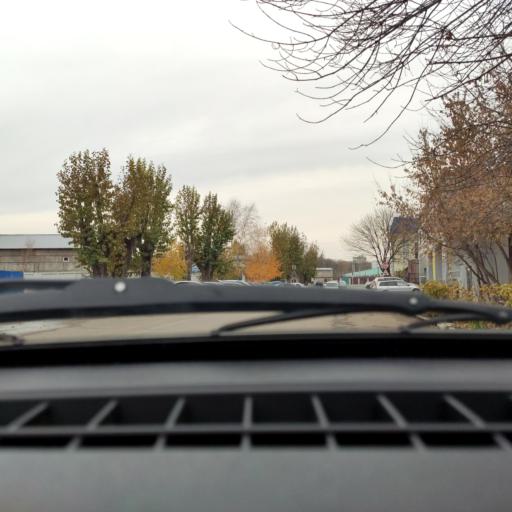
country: RU
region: Bashkortostan
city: Ufa
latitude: 54.7895
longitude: 56.0612
